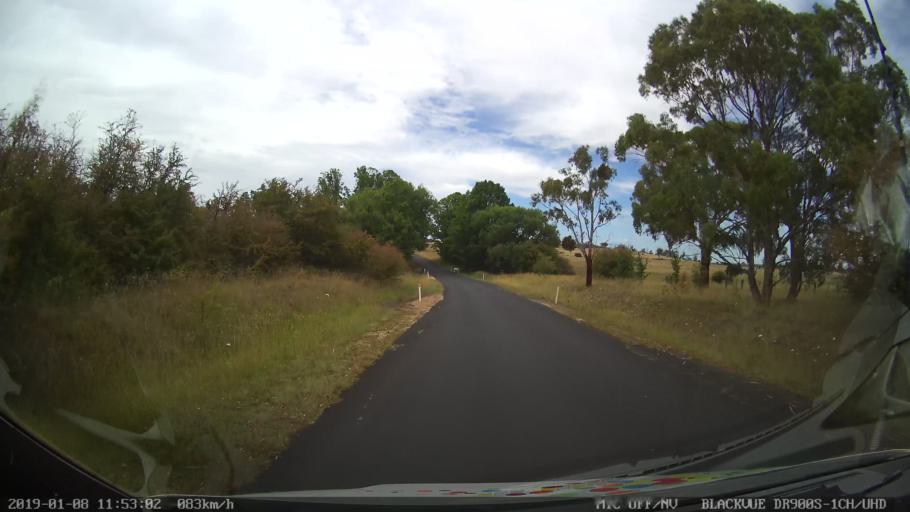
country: AU
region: New South Wales
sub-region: Armidale Dumaresq
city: Armidale
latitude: -30.4100
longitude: 151.5595
